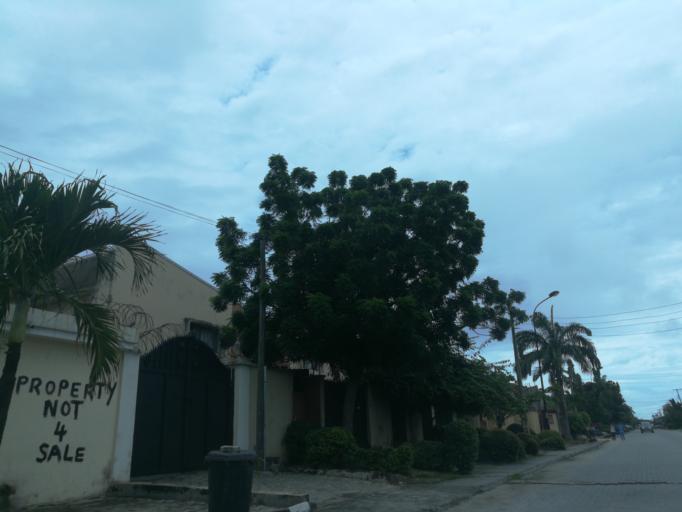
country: NG
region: Lagos
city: Ikoyi
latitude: 6.4458
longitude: 3.4641
